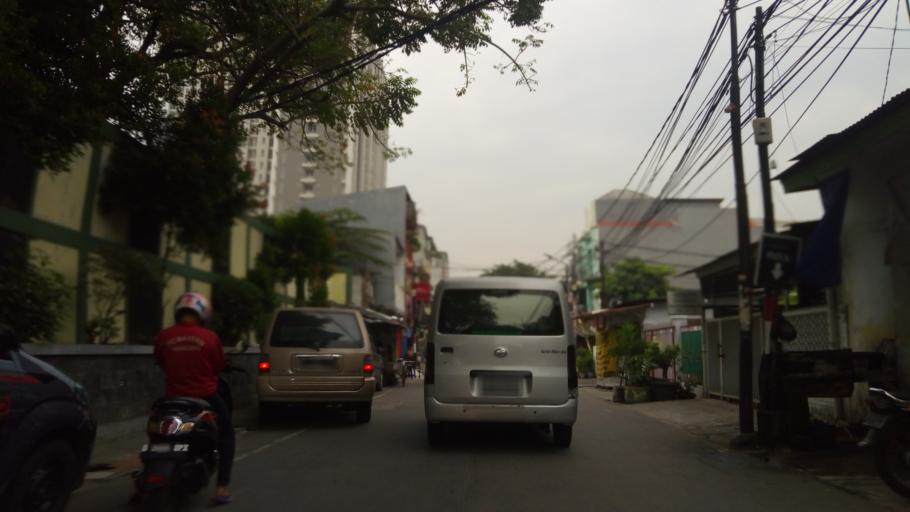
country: ID
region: Jakarta Raya
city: Jakarta
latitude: -6.1504
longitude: 106.8360
